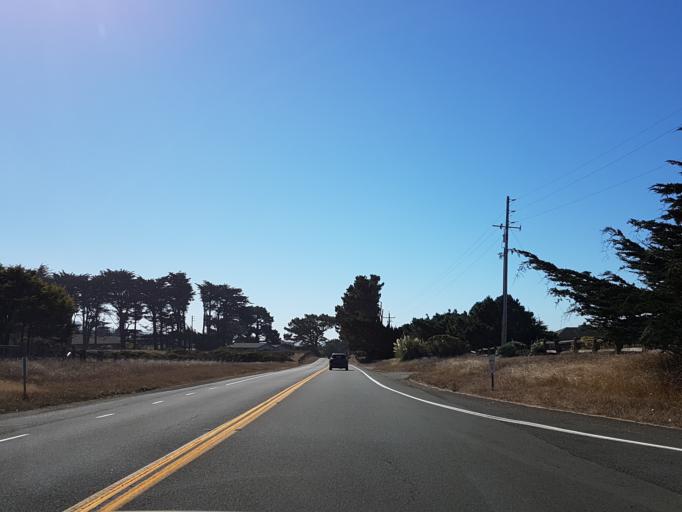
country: US
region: California
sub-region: Mendocino County
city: Boonville
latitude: 39.0282
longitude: -123.6883
